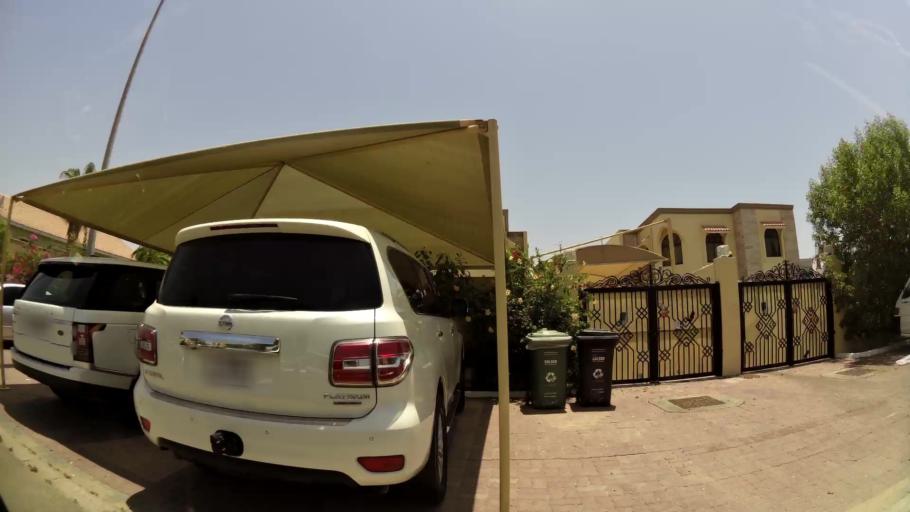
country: AE
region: Dubai
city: Dubai
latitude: 25.2108
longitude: 55.2501
